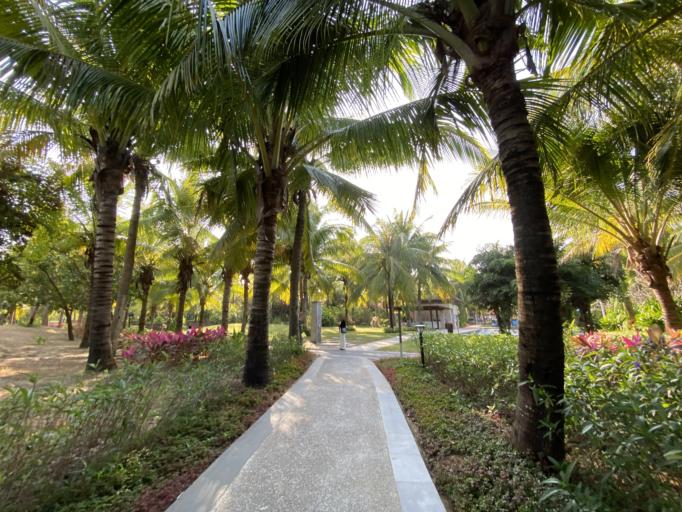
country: CN
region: Hainan
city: Haitangwan
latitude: 18.3489
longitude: 109.7397
